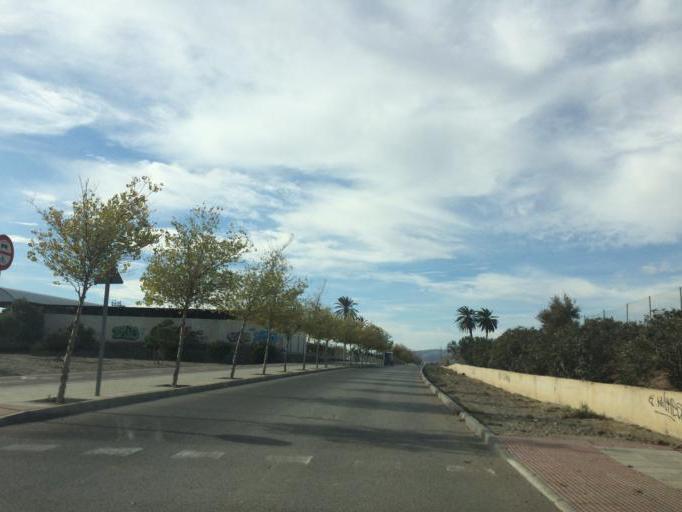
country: ES
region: Andalusia
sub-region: Provincia de Almeria
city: Almeria
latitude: 36.8323
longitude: -2.4287
